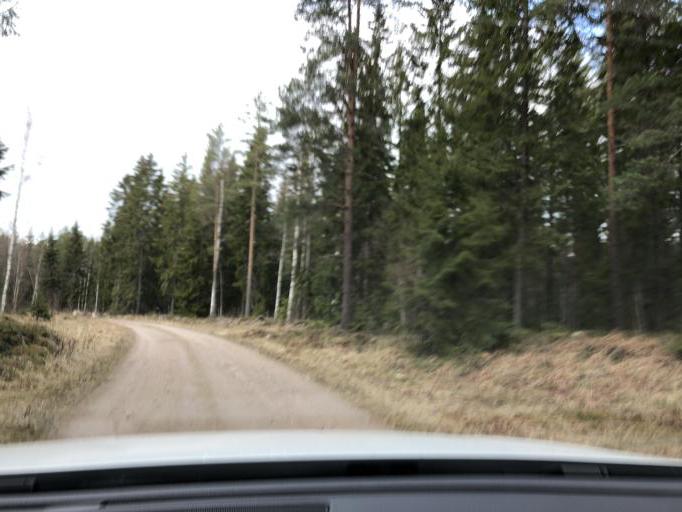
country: SE
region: Gaevleborg
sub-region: Gavle Kommun
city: Hedesunda
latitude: 60.3418
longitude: 17.1047
